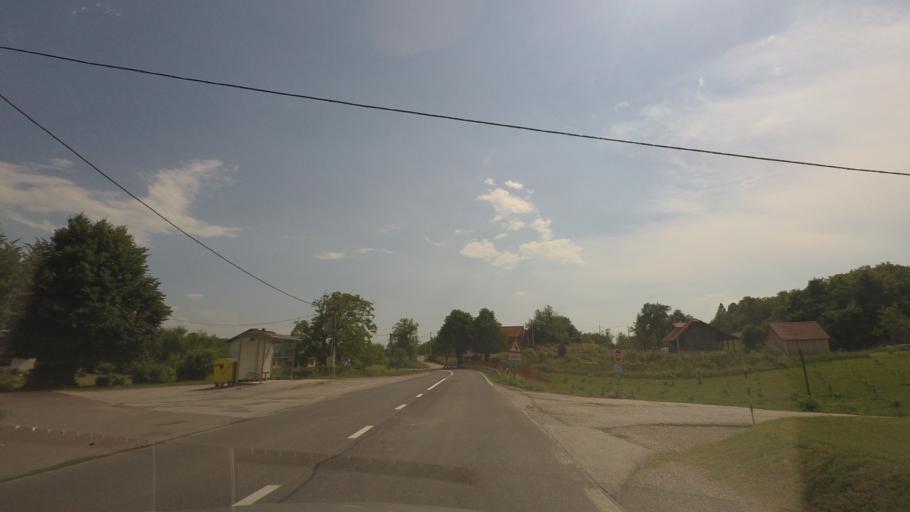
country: HR
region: Karlovacka
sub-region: Grad Karlovac
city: Karlovac
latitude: 45.4168
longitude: 15.4566
